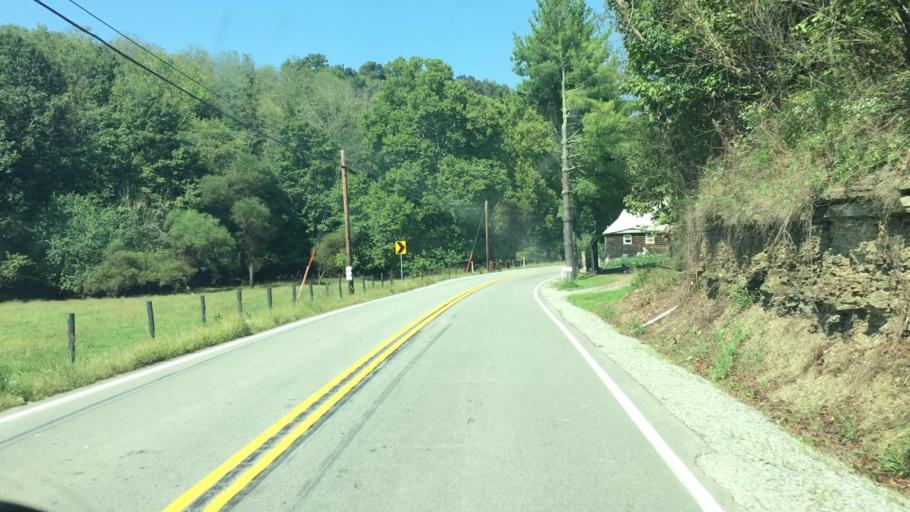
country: US
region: Pennsylvania
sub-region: Greene County
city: Waynesburg
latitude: 39.9412
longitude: -80.2885
